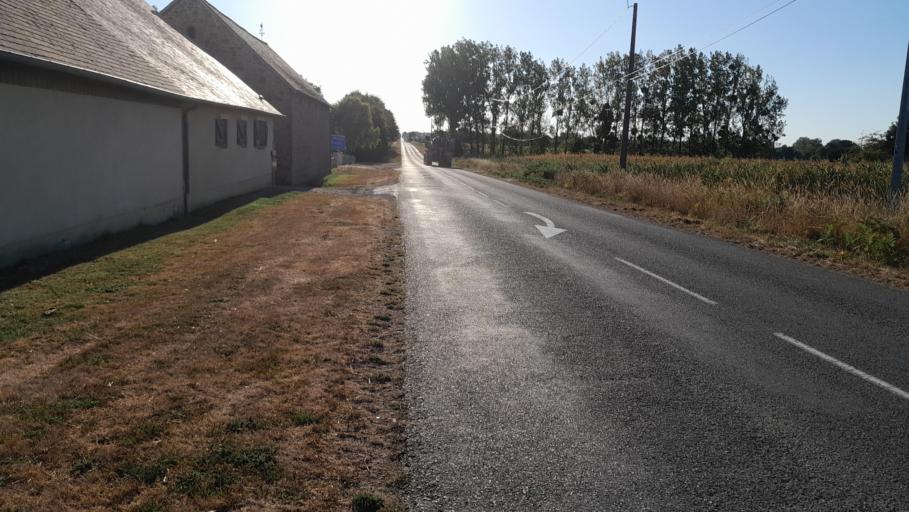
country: FR
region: Brittany
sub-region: Departement d'Ille-et-Vilaine
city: Le Pertre
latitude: 47.9667
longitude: -1.0616
